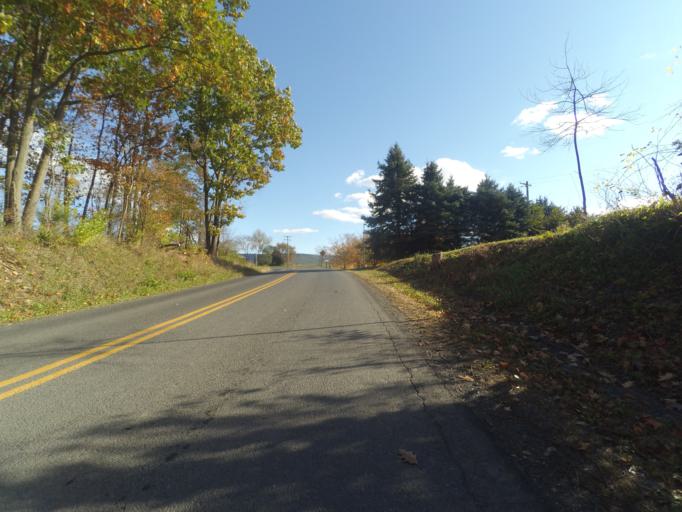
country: US
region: Pennsylvania
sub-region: Centre County
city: Bellefonte
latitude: 40.8788
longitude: -77.7814
